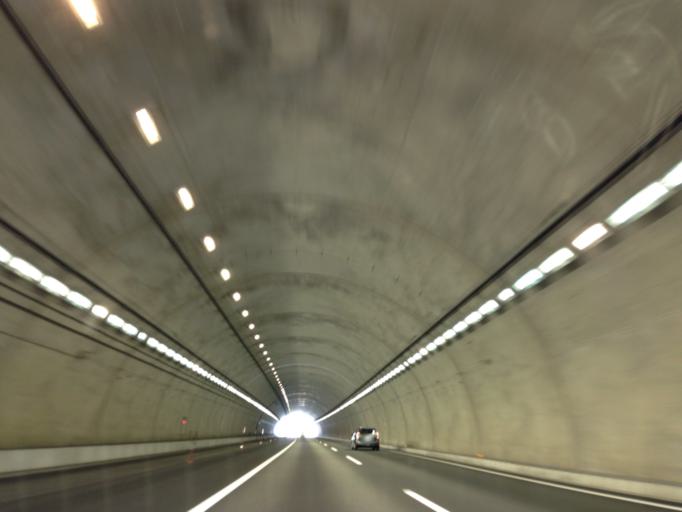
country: JP
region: Shizuoka
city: Mishima
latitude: 35.1829
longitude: 138.8873
